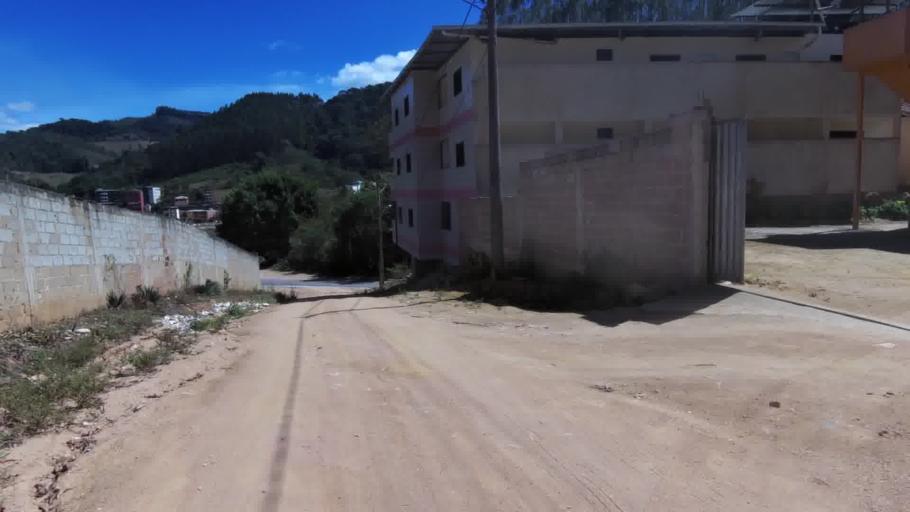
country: BR
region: Espirito Santo
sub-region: Vargem Alta
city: Vargem Alta
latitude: -20.6734
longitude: -41.0043
